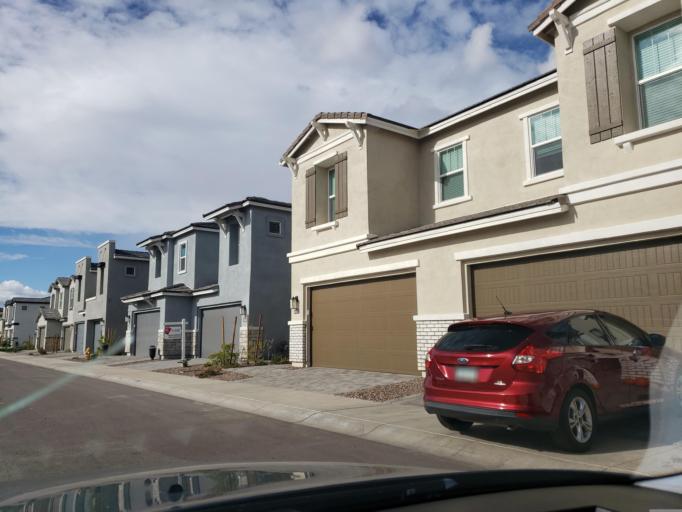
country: US
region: Arizona
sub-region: Maricopa County
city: Paradise Valley
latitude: 33.6445
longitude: -111.9754
